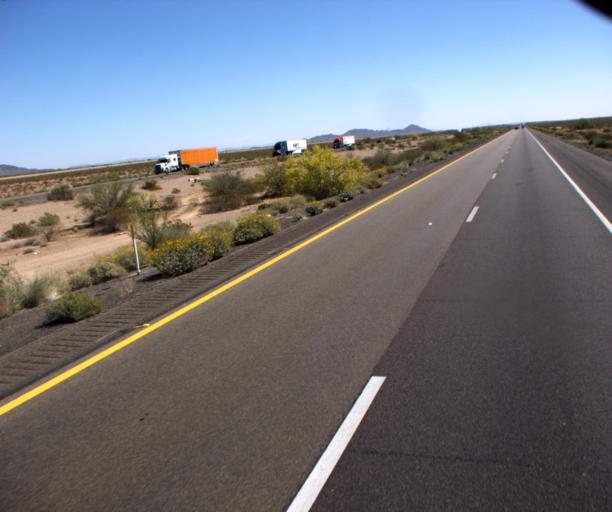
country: US
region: Arizona
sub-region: La Paz County
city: Salome
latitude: 33.6002
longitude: -113.5625
